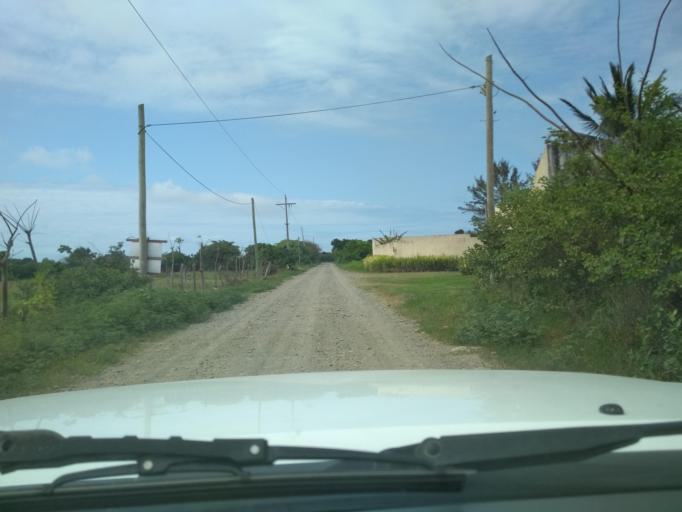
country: MX
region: Veracruz
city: Anton Lizardo
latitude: 19.0288
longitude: -95.9696
